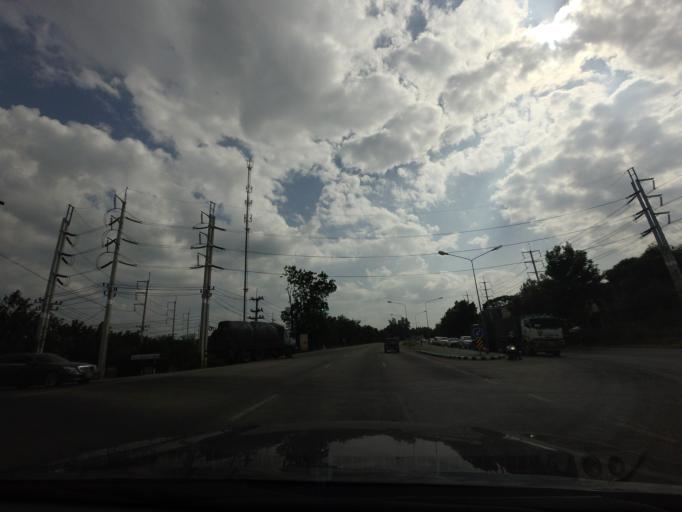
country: TH
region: Lop Buri
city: Chai Badan
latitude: 15.2171
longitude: 101.1272
